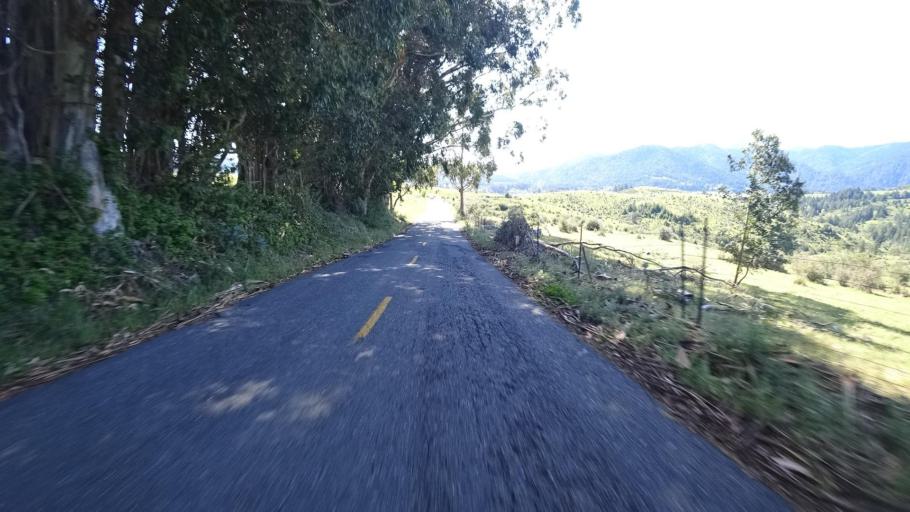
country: US
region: California
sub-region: Humboldt County
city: Ferndale
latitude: 40.3348
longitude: -124.3058
